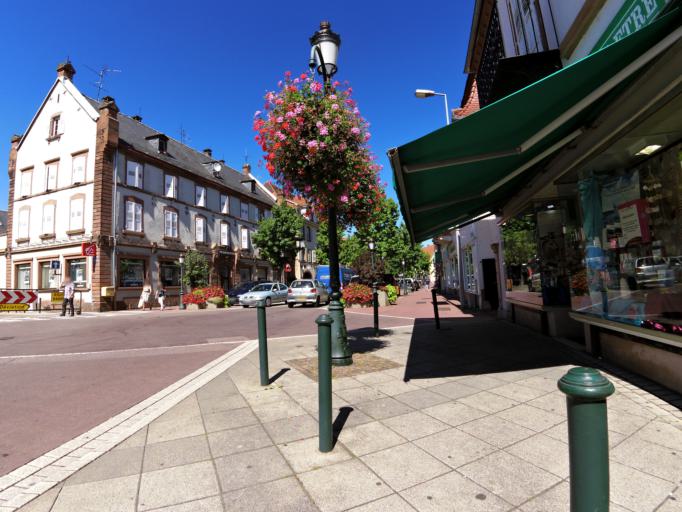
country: FR
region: Alsace
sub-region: Departement du Bas-Rhin
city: Haguenau
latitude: 48.8162
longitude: 7.7919
